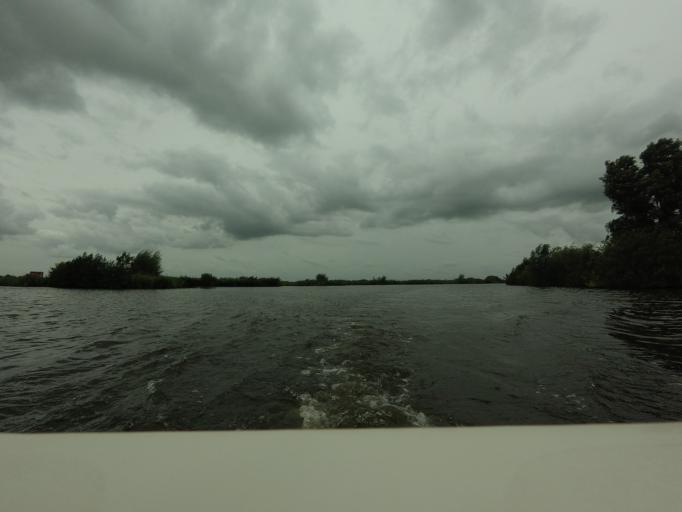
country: NL
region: Friesland
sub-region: Gemeente Boarnsterhim
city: Aldeboarn
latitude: 53.0946
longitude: 5.9221
